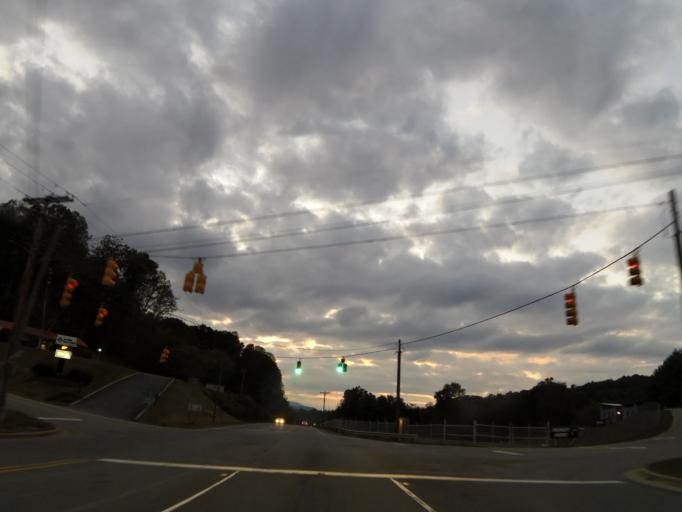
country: US
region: North Carolina
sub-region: Madison County
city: Marshall
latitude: 35.8137
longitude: -82.6739
